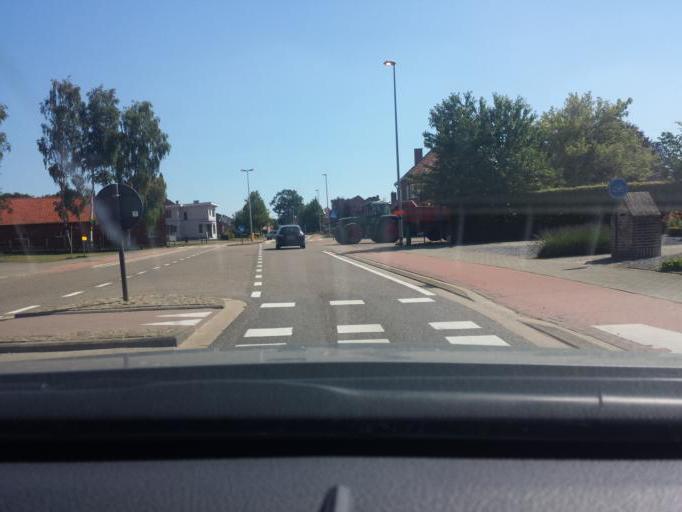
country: BE
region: Flanders
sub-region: Provincie Limburg
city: Lummen
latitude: 51.0111
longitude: 5.2031
